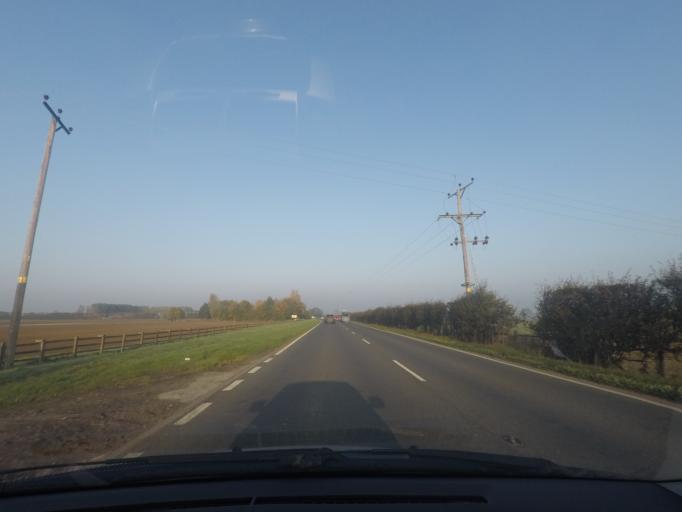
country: GB
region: England
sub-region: City of York
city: Askham Richard
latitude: 53.9905
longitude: -1.2332
